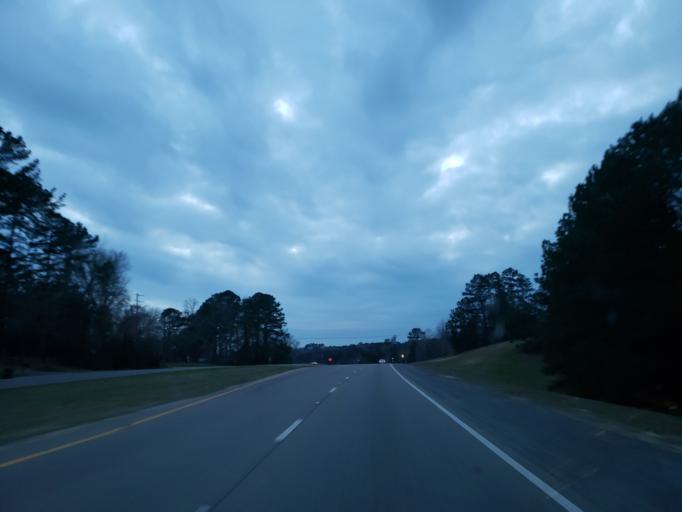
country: US
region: Mississippi
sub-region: Lauderdale County
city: Marion
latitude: 32.3671
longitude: -88.6447
